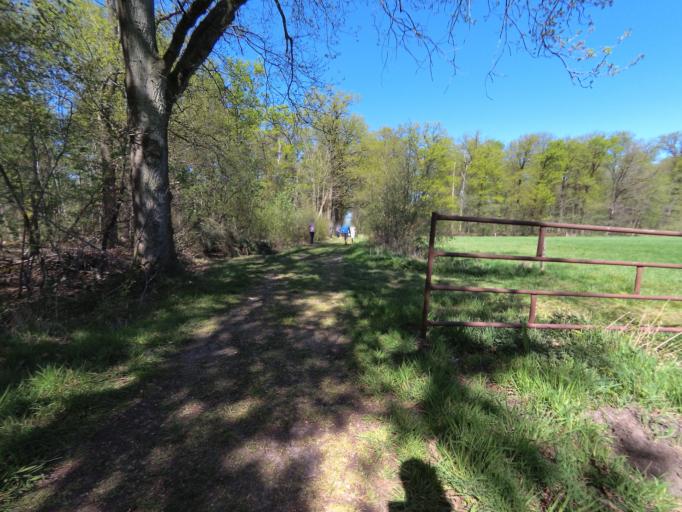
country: NL
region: Utrecht
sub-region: Gemeente Woudenberg
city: Woudenberg
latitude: 52.0904
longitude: 5.4104
